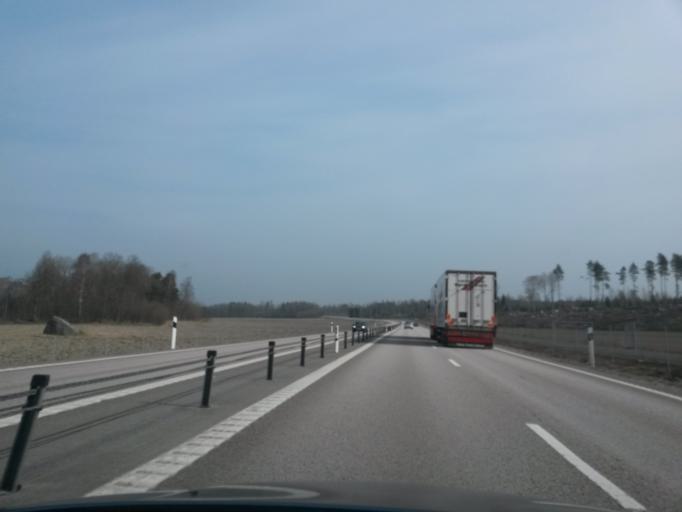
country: SE
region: Vaestra Goetaland
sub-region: Mariestads Kommun
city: Mariestad
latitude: 58.7547
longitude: 13.9626
